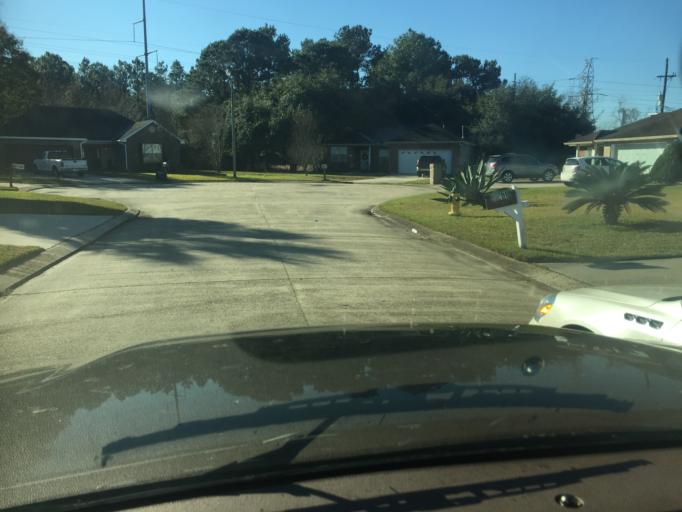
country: US
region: Louisiana
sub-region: Saint Tammany Parish
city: Slidell
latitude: 30.2525
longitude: -89.7601
